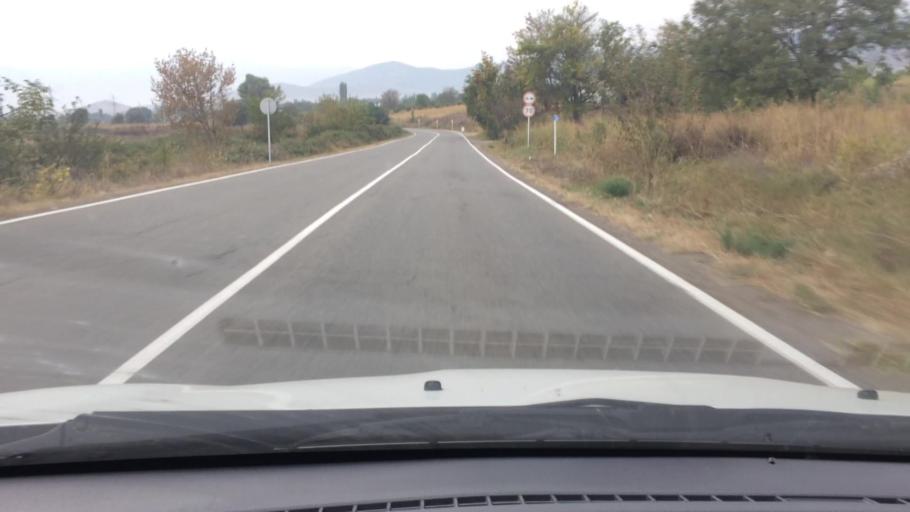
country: GE
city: Naghvarevi
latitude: 41.3178
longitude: 44.7944
